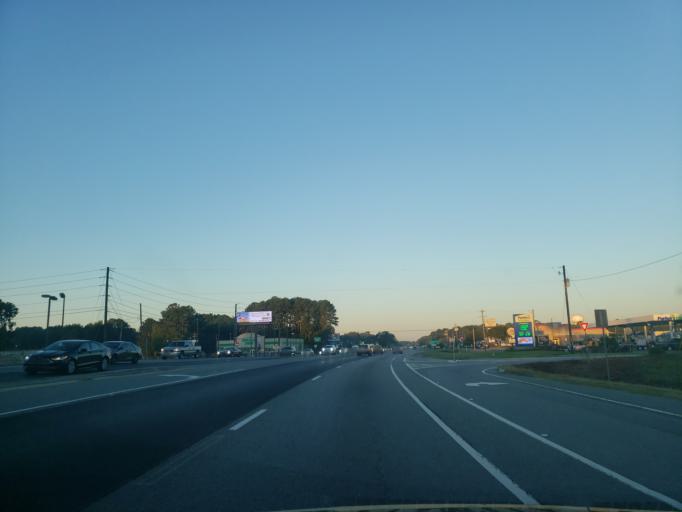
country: US
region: Georgia
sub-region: Chatham County
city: Georgetown
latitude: 31.9986
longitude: -81.2512
